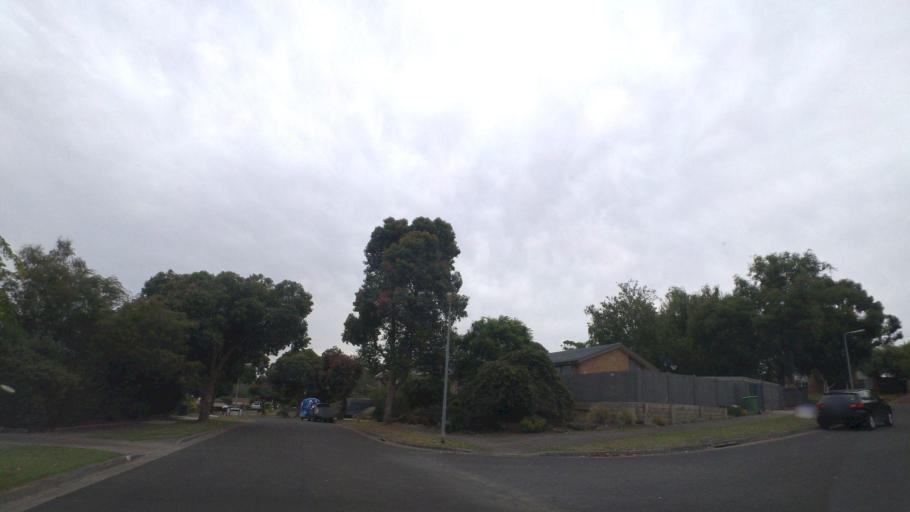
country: AU
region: Victoria
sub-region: Yarra Ranges
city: Lilydale
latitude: -37.7767
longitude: 145.3361
